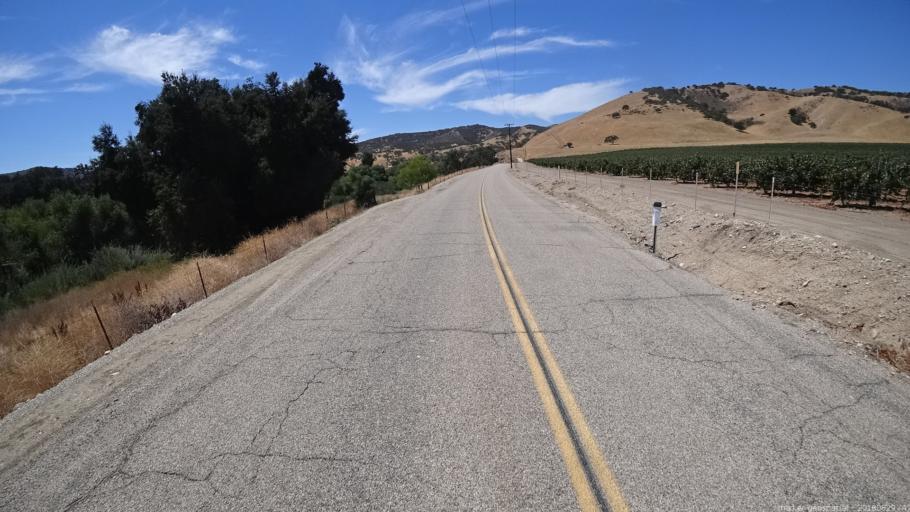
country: US
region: California
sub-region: San Luis Obispo County
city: Lake Nacimiento
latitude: 35.8091
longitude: -120.8518
